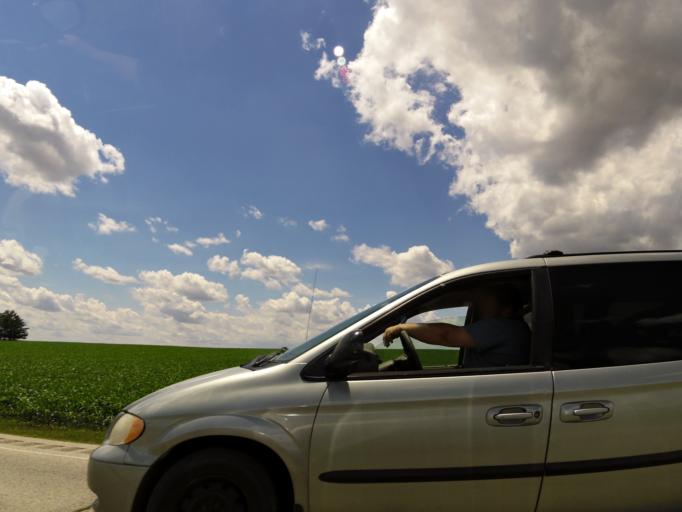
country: US
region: Iowa
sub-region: Buchanan County
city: Independence
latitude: 42.5261
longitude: -91.8899
